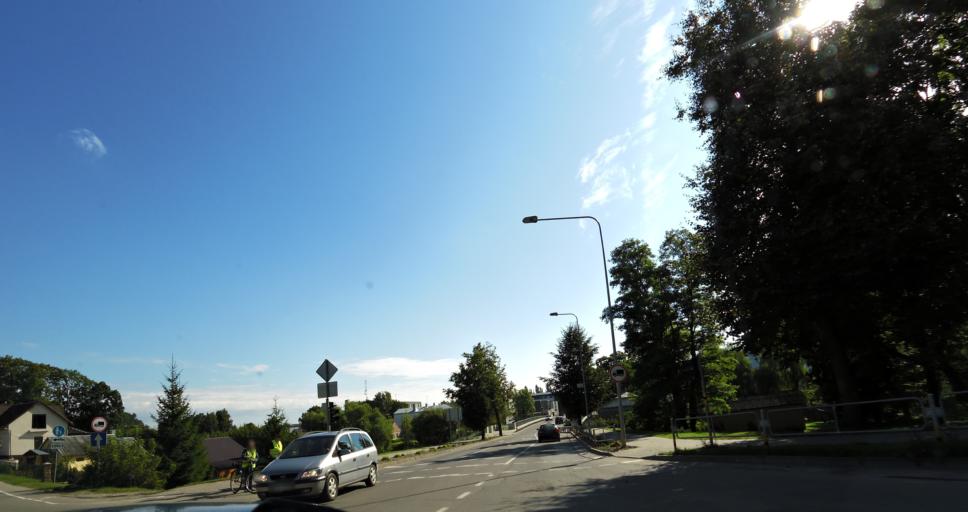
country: LT
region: Panevezys
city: Pasvalys
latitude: 56.0629
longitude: 24.3957
